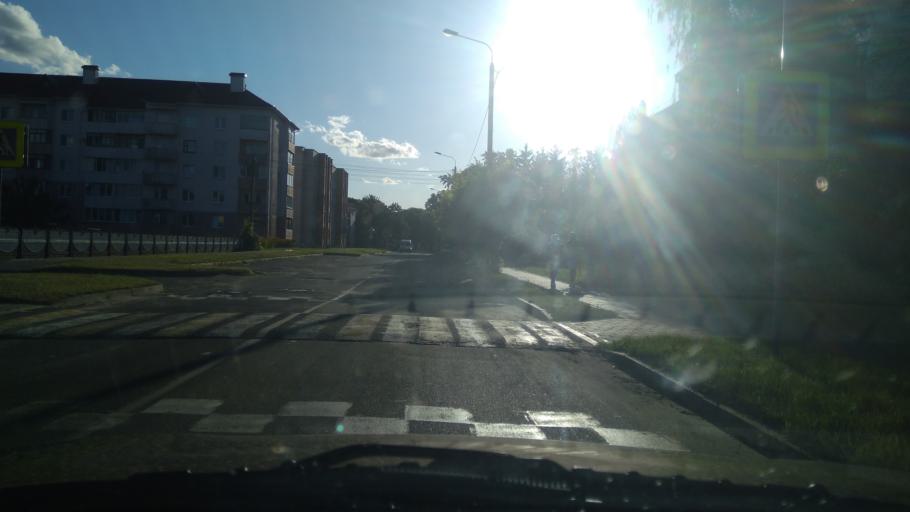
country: BY
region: Brest
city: Pruzhany
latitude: 52.5641
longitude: 24.4605
